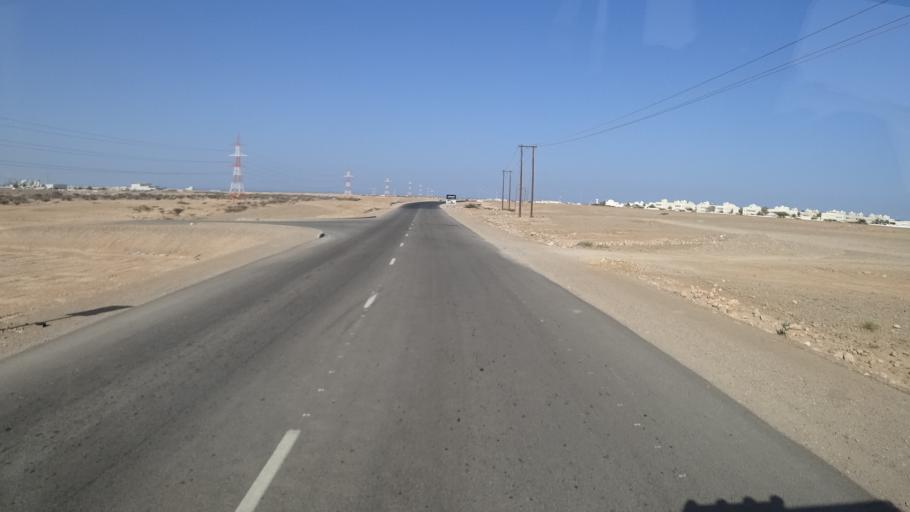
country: OM
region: Ash Sharqiyah
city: Sur
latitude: 22.6053
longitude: 59.4316
